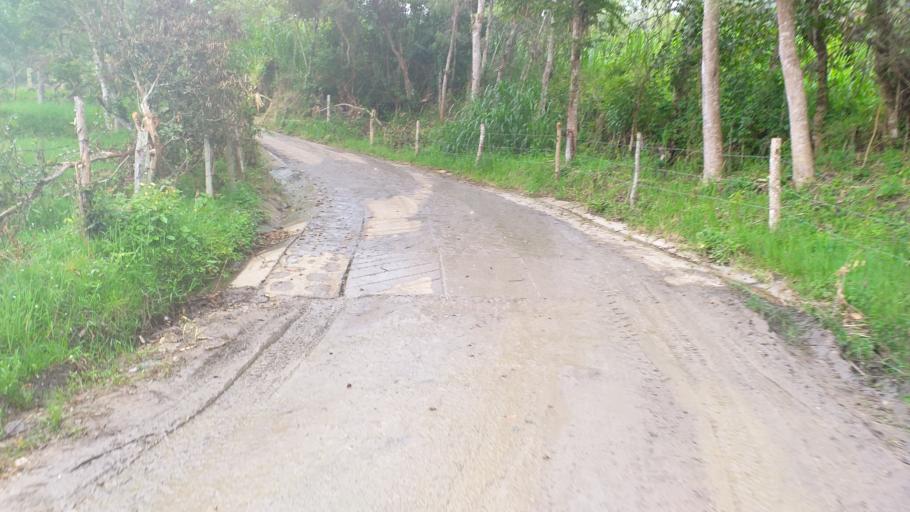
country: CO
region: Cundinamarca
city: Tenza
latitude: 5.0878
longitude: -73.4554
